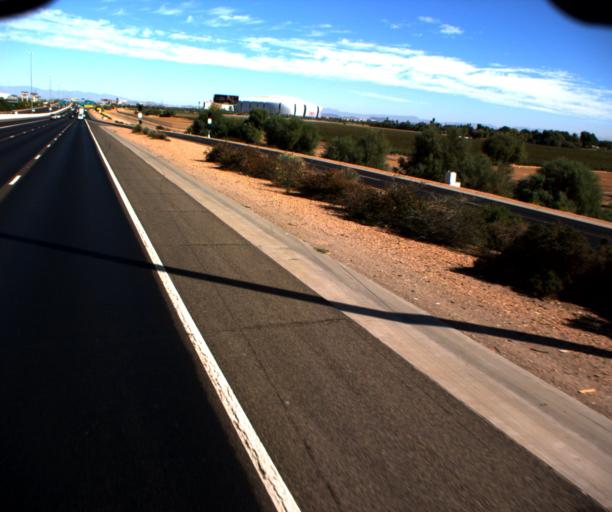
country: US
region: Arizona
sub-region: Maricopa County
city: Tolleson
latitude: 33.5110
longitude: -112.2690
